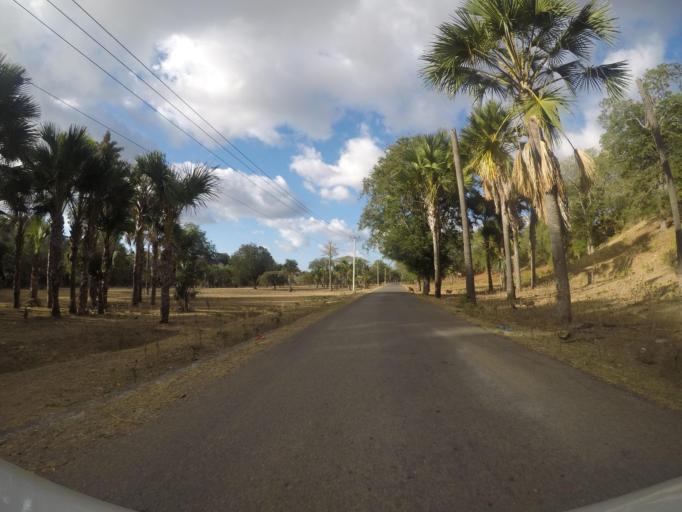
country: TL
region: Lautem
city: Lospalos
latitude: -8.4103
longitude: 126.8268
